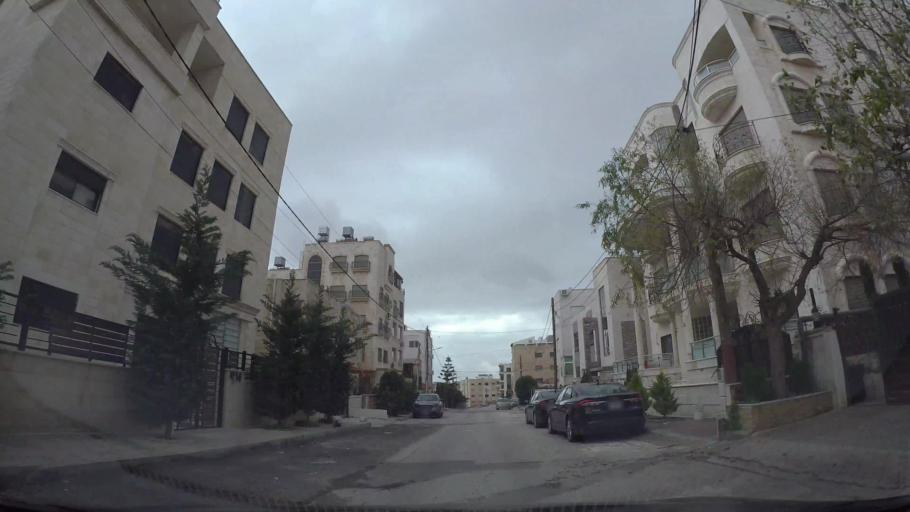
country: JO
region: Amman
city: Wadi as Sir
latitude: 31.9654
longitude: 35.8300
